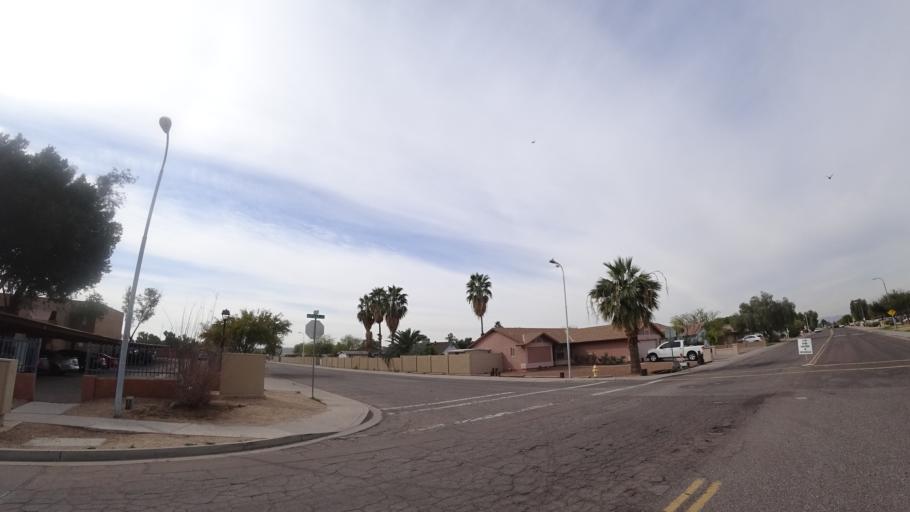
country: US
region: Arizona
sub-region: Maricopa County
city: Glendale
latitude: 33.5346
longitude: -112.2073
